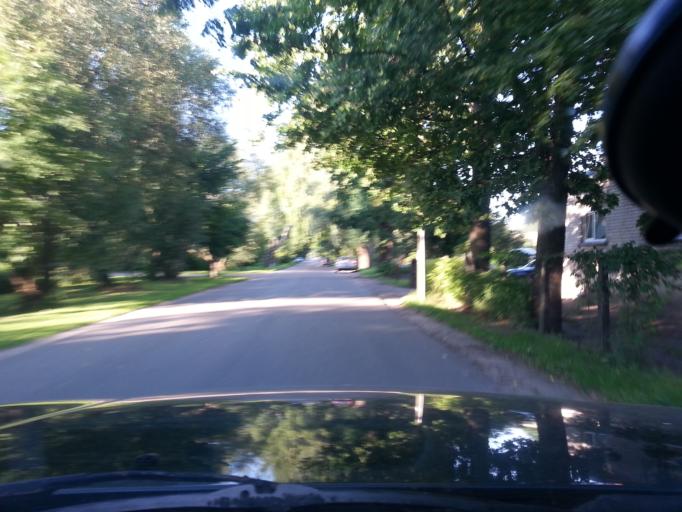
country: LV
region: Riga
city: Riga
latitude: 56.9390
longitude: 24.1857
